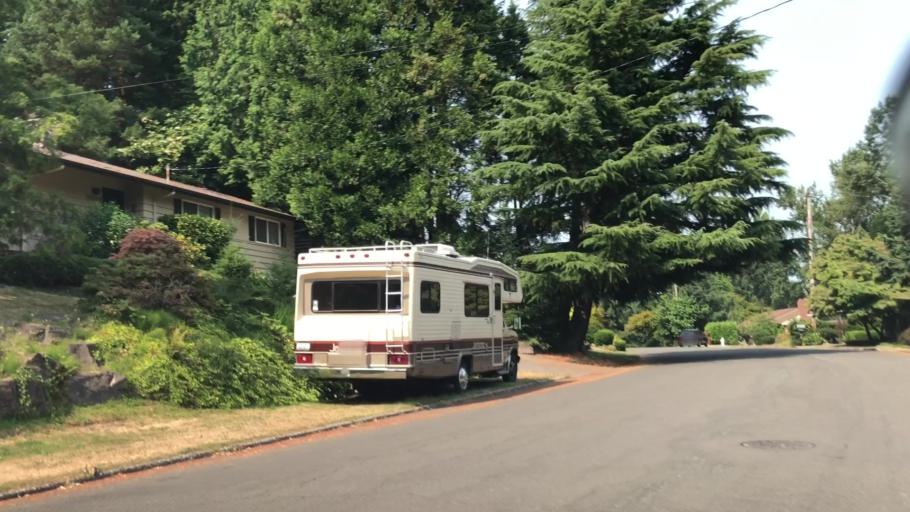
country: US
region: Washington
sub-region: King County
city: Kenmore
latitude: 47.7612
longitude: -122.2536
